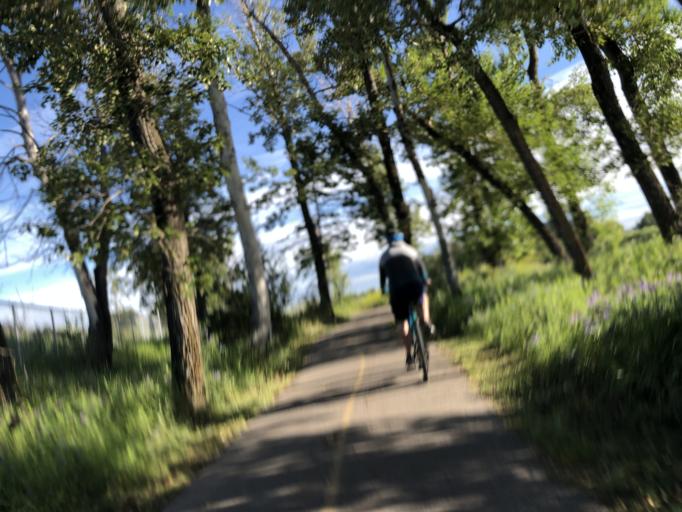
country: CA
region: Alberta
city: Calgary
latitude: 50.9538
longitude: -114.0218
